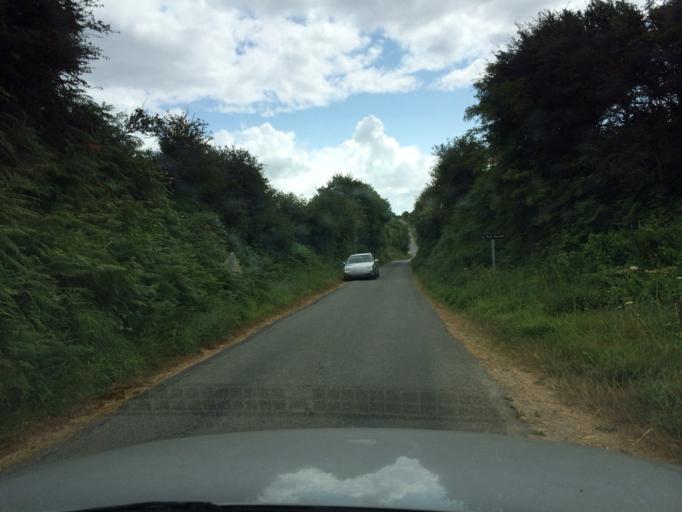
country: FR
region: Lower Normandy
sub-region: Departement de la Manche
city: Beaumont-Hague
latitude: 49.6849
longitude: -1.8673
